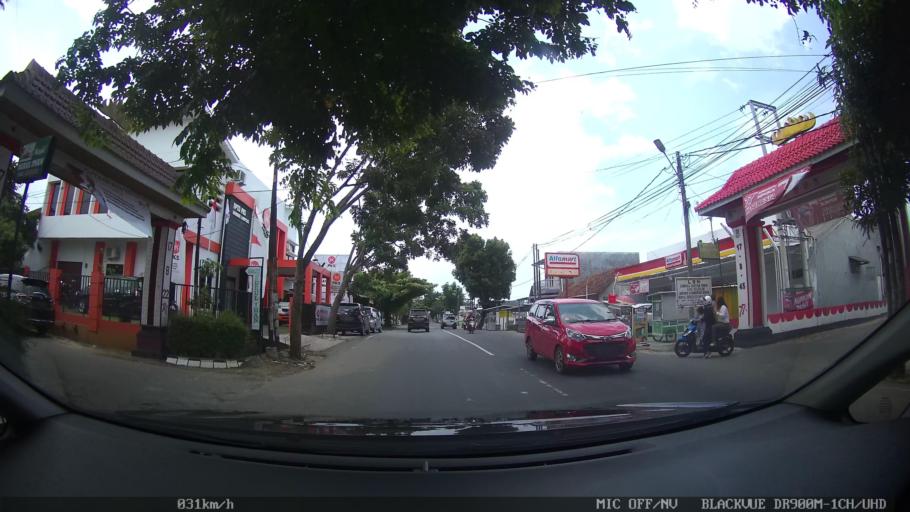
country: ID
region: Lampung
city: Bandarlampung
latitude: -5.4045
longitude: 105.2418
